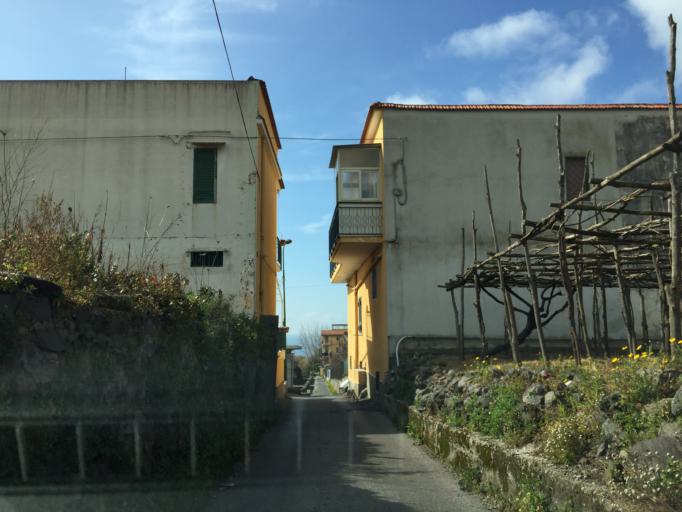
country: IT
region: Campania
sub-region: Provincia di Napoli
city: Torre del Greco
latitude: 40.7783
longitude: 14.4139
